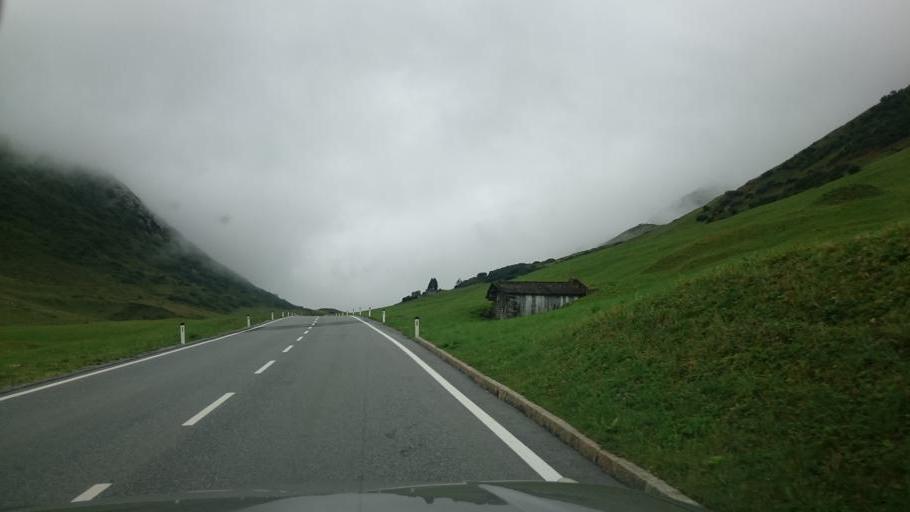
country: AT
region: Vorarlberg
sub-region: Politischer Bezirk Bludenz
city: Lech
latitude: 47.1648
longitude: 10.1641
